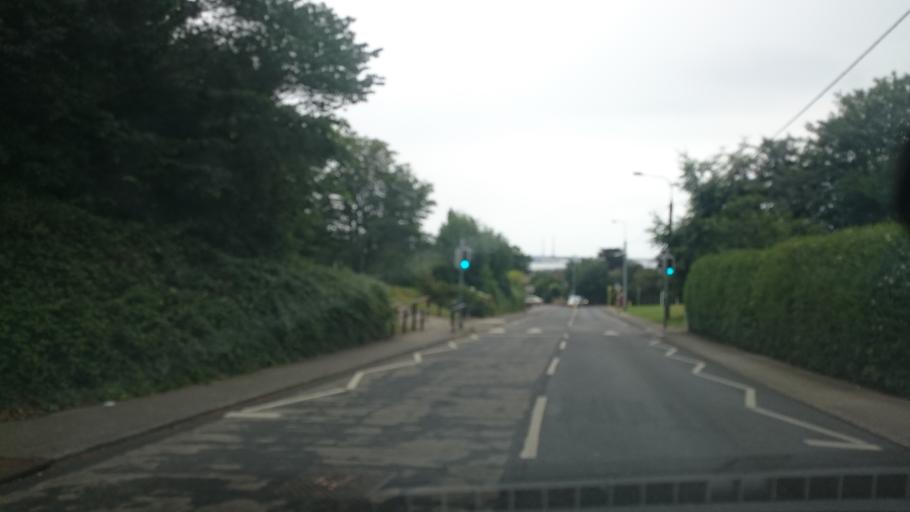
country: IE
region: Leinster
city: Mount Merrion
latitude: 53.2954
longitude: -6.2108
